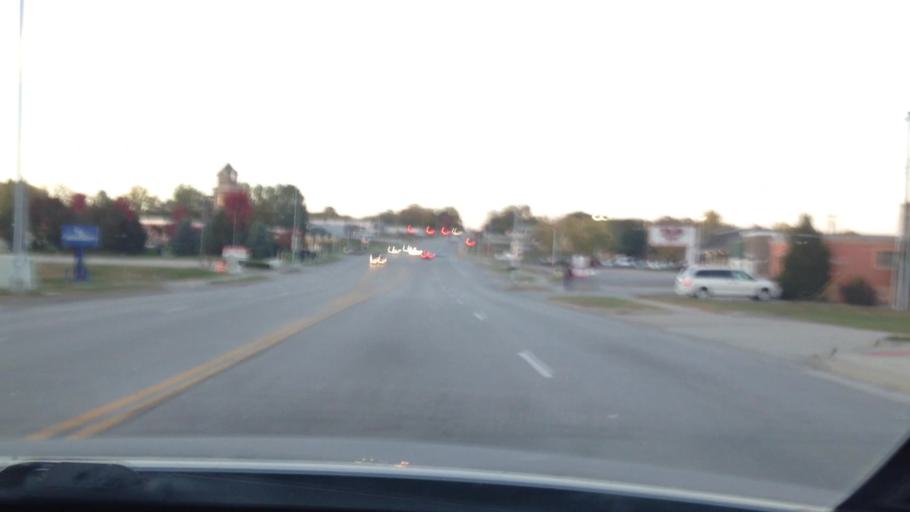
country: US
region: Missouri
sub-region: Platte County
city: Riverside
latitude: 39.1756
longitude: -94.6131
